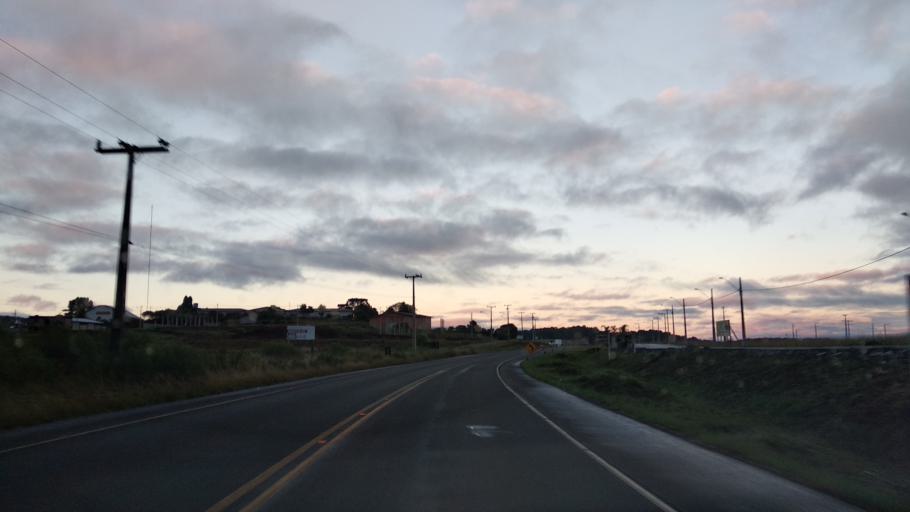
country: BR
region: Santa Catarina
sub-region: Campos Novos
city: Campos Novos
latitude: -27.3765
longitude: -51.2051
